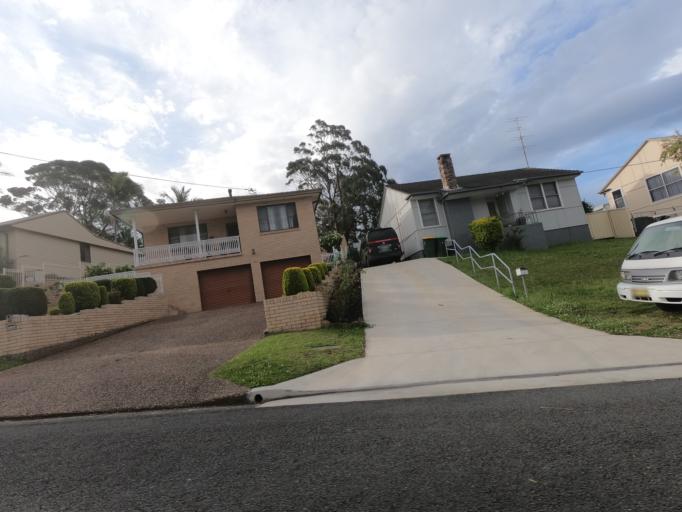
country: AU
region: New South Wales
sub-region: Wollongong
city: Berkeley
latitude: -34.4778
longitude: 150.8445
